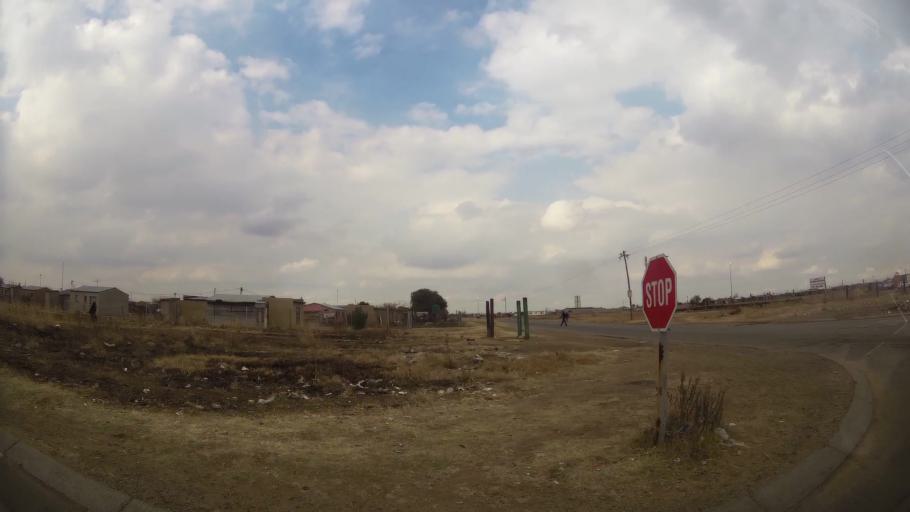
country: ZA
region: Orange Free State
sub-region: Fezile Dabi District Municipality
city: Sasolburg
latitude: -26.8539
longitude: 27.8734
